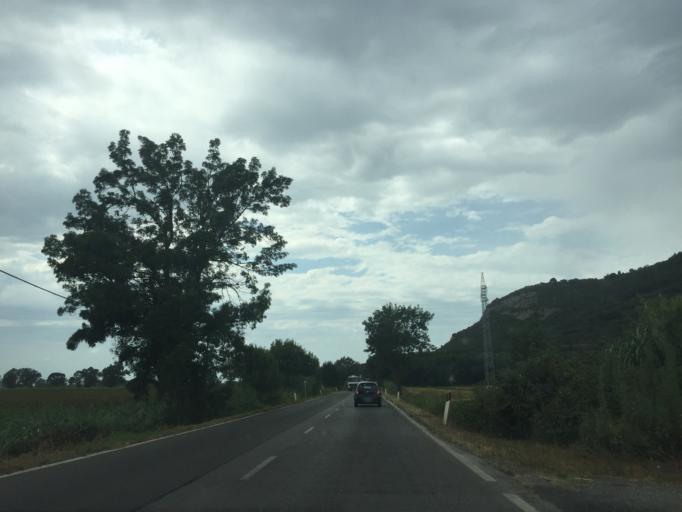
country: IT
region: Tuscany
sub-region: Province of Pisa
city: Asciano
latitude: 43.7492
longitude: 10.4590
